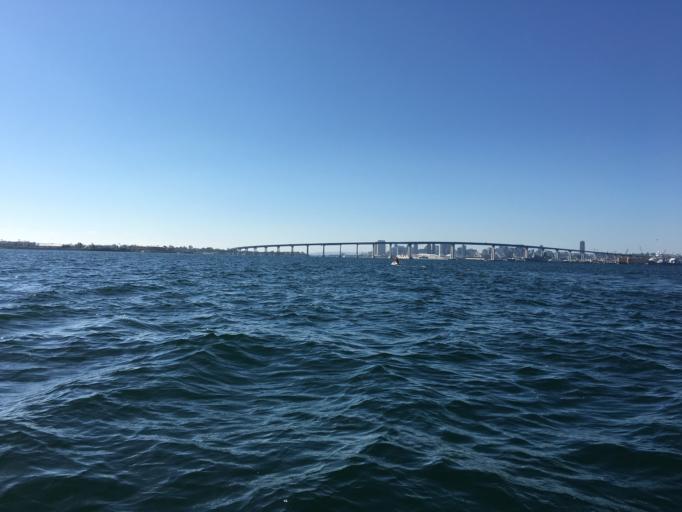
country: US
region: California
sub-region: San Diego County
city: Coronado
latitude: 32.6693
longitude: -117.1431
